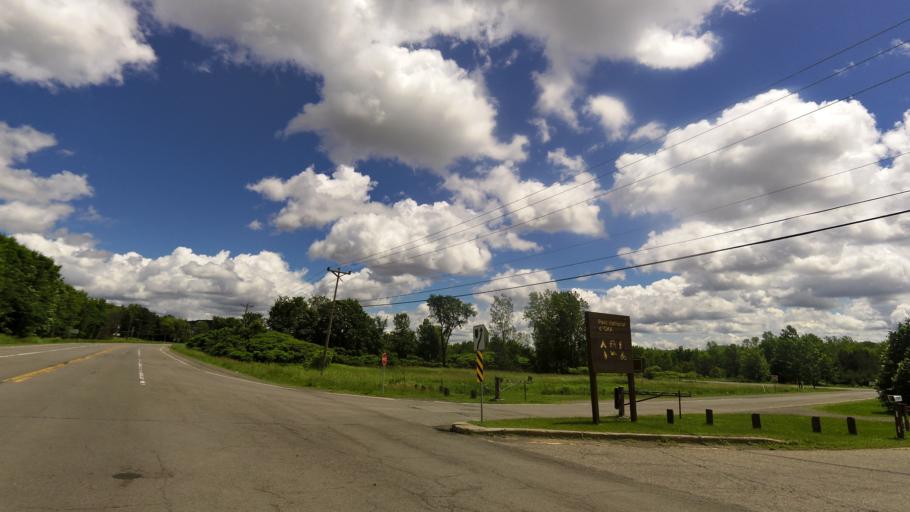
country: CA
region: Quebec
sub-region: Laurentides
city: Oka
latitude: 45.4758
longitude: -74.0613
